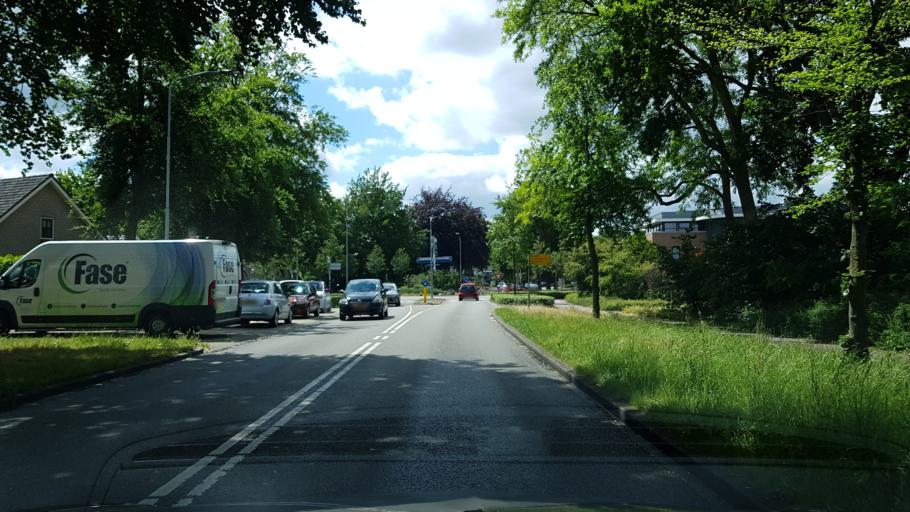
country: NL
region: Gelderland
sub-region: Gemeente Nunspeet
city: Nunspeet
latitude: 52.3754
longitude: 5.7710
